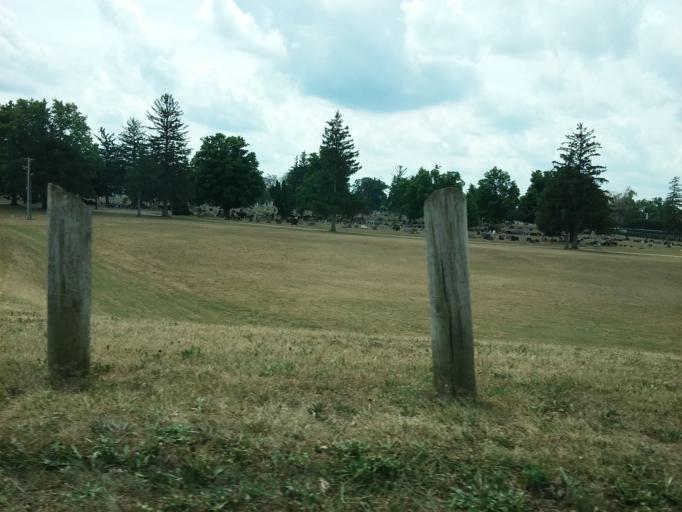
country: US
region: Ohio
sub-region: Hancock County
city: Findlay
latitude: 41.0486
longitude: -83.6649
